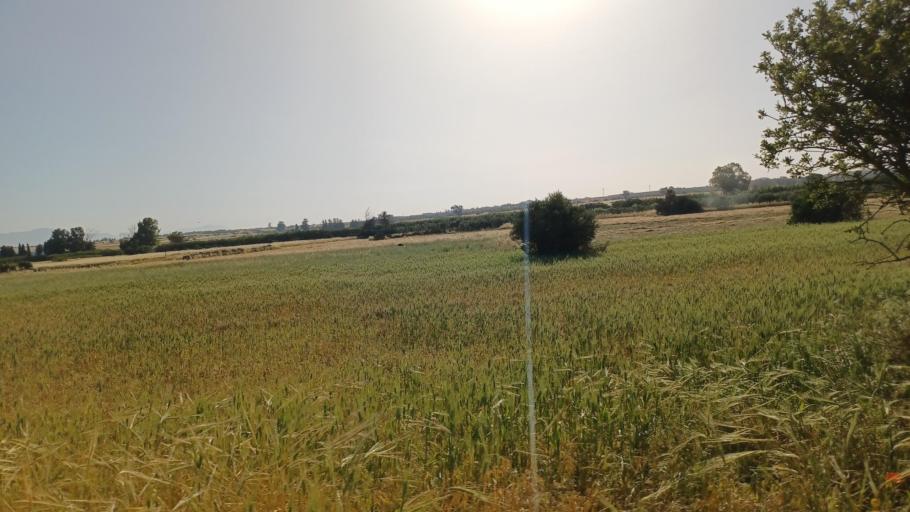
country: CY
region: Lefkosia
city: Mammari
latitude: 35.1621
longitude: 33.2467
